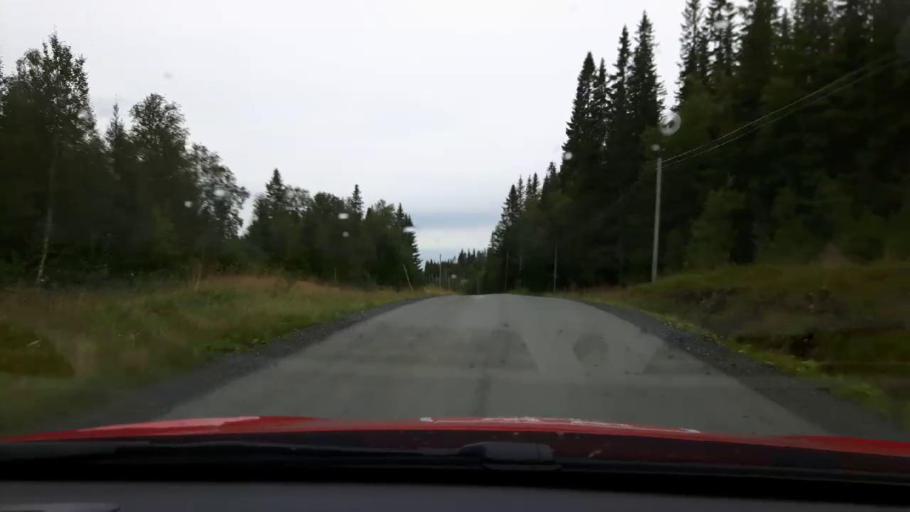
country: SE
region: Jaemtland
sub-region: Are Kommun
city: Are
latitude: 63.4689
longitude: 13.1742
